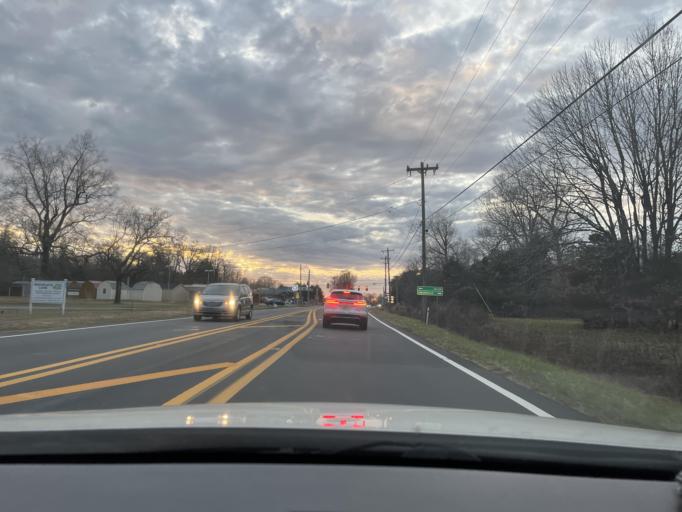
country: US
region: North Carolina
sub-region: Guilford County
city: Gibsonville
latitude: 36.0778
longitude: -79.5629
